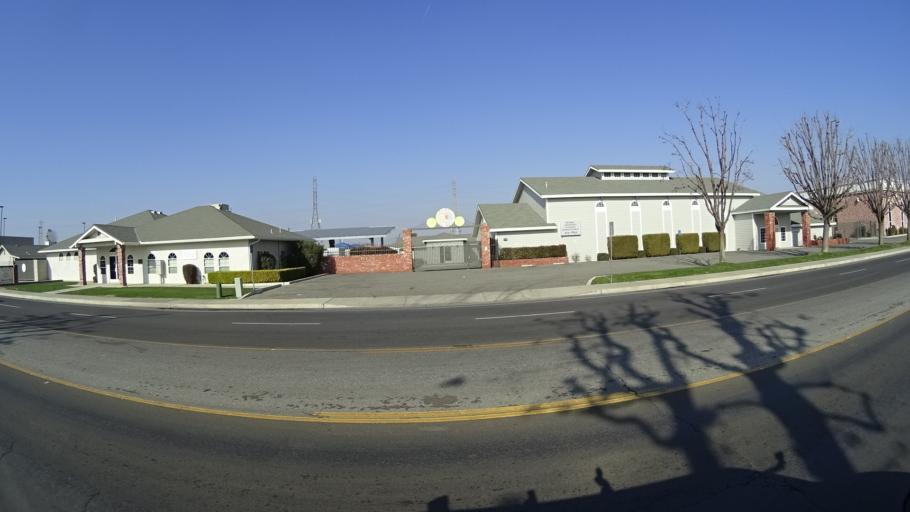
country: US
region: California
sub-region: Kern County
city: Oildale
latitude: 35.3980
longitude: -119.0174
